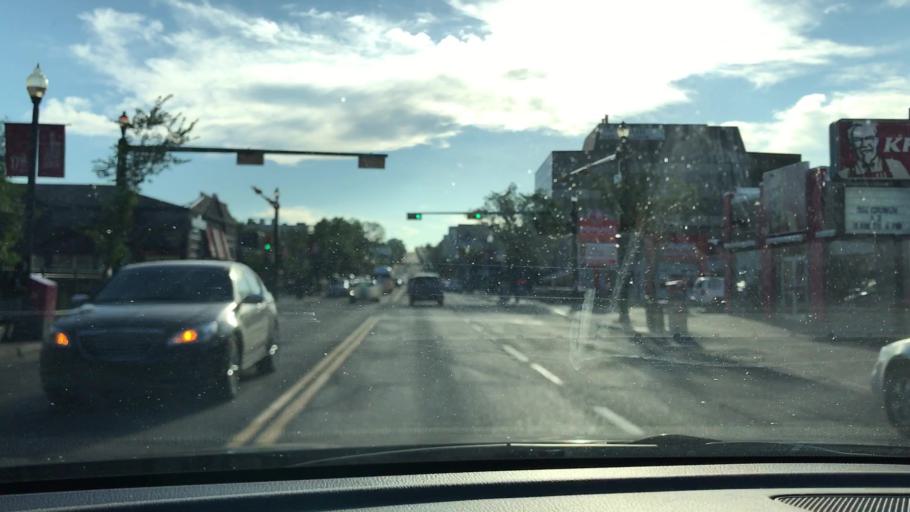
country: CA
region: Alberta
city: Calgary
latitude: 51.0379
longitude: -114.0911
